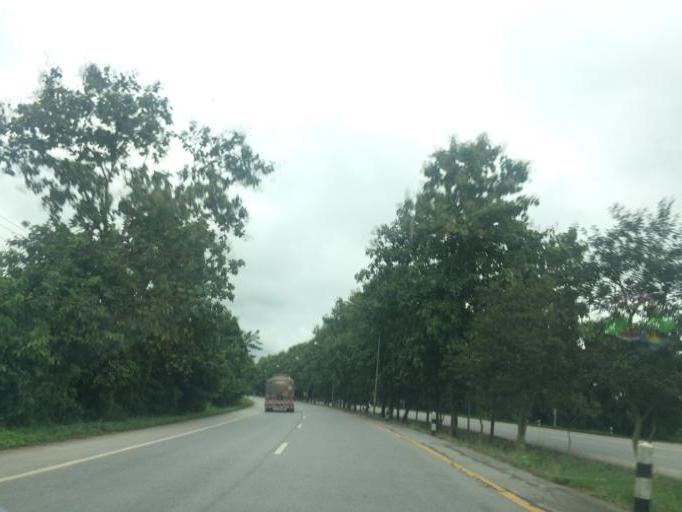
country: TH
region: Chiang Rai
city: Mae Lao
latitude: 19.8001
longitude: 99.7532
